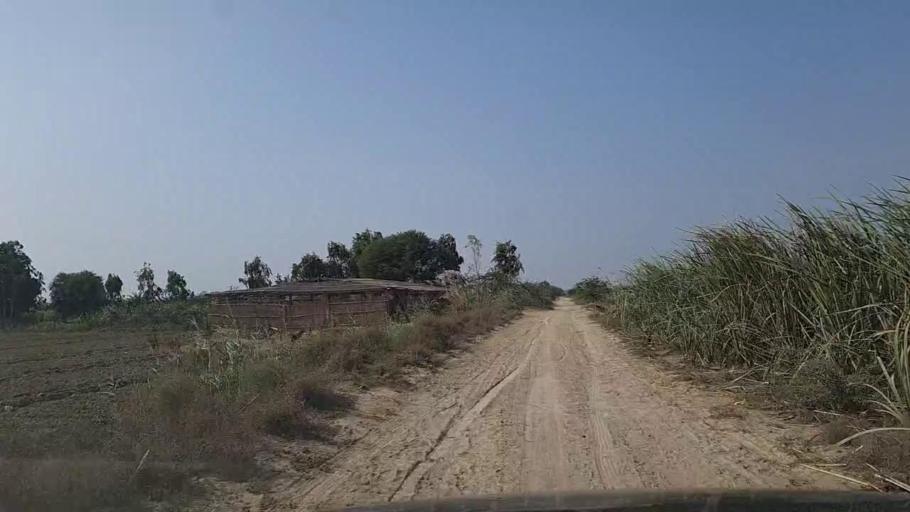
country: PK
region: Sindh
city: Gharo
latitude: 24.7313
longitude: 67.7289
